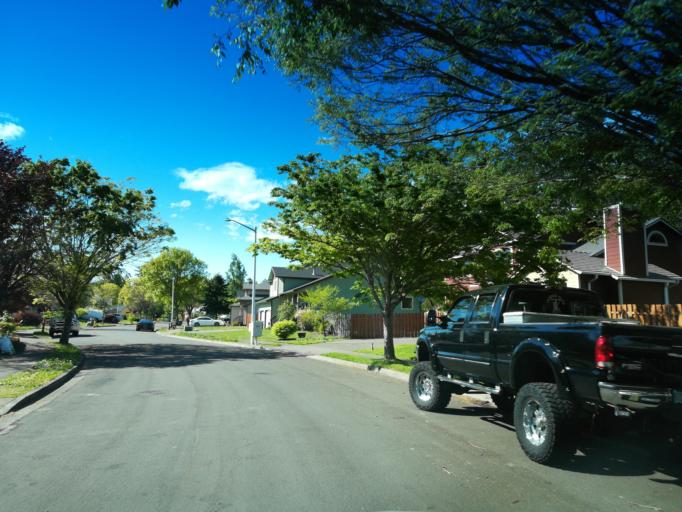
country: US
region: Oregon
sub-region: Multnomah County
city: Troutdale
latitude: 45.5350
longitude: -122.3808
